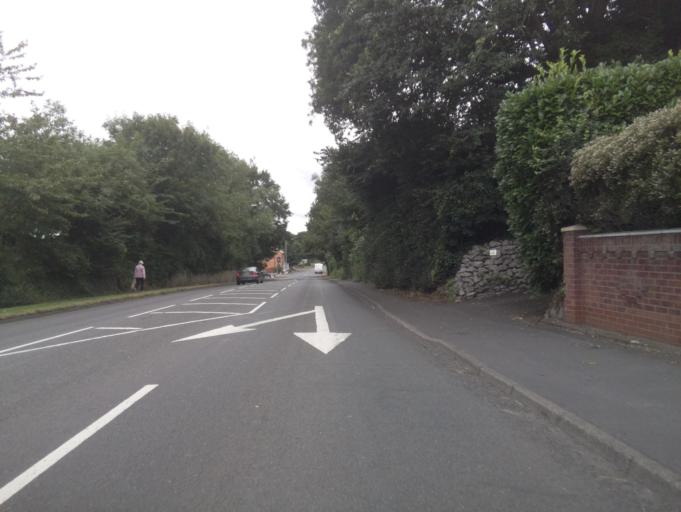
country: GB
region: England
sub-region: Worcestershire
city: Droitwich
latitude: 52.2556
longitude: -2.1580
